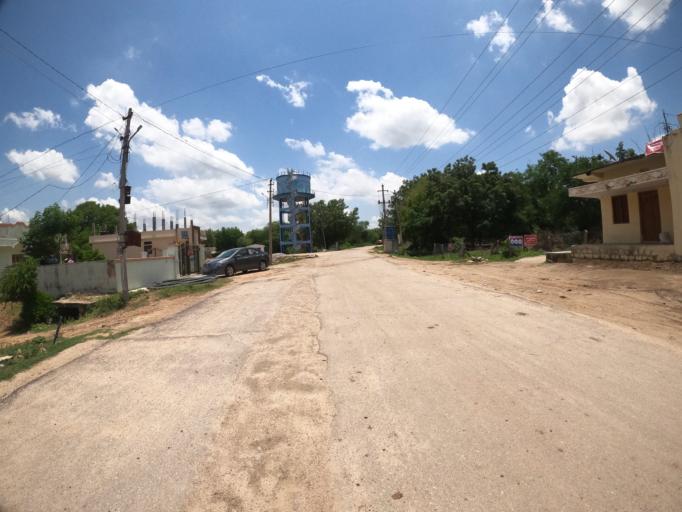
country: IN
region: Telangana
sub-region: Rangareddi
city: Singapur
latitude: 17.4420
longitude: 78.1573
